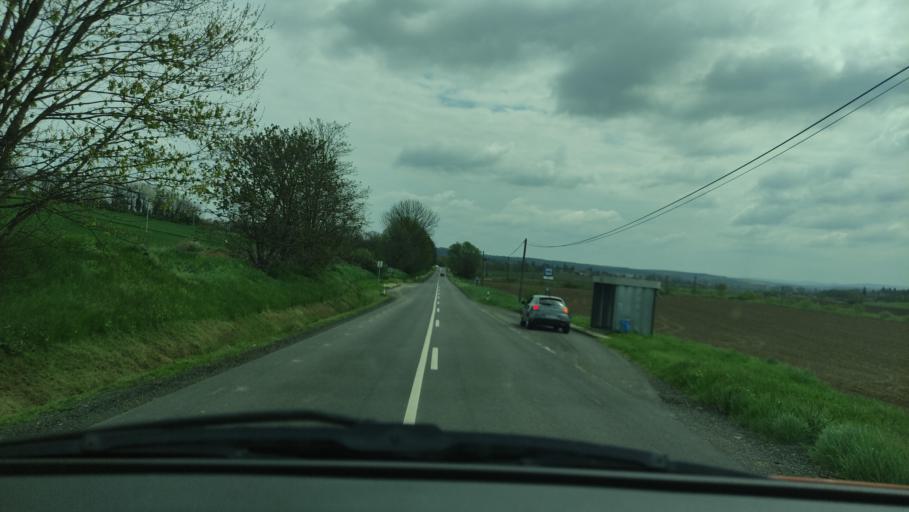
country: HU
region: Baranya
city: Sasd
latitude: 46.2660
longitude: 18.0794
